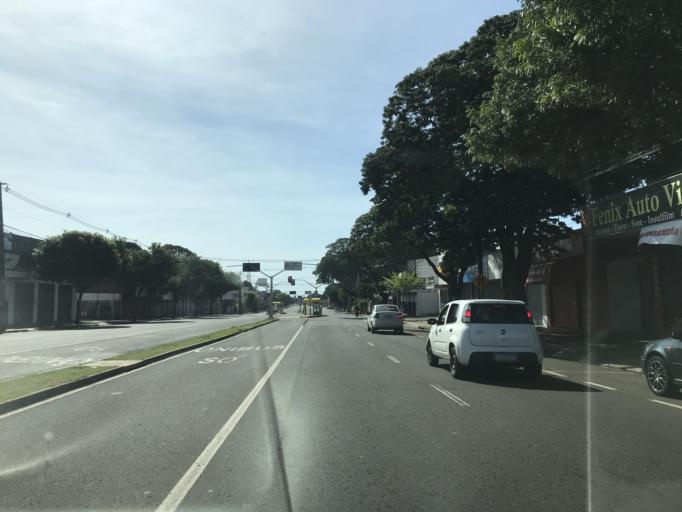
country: BR
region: Parana
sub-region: Maringa
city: Maringa
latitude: -23.4063
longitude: -51.9298
